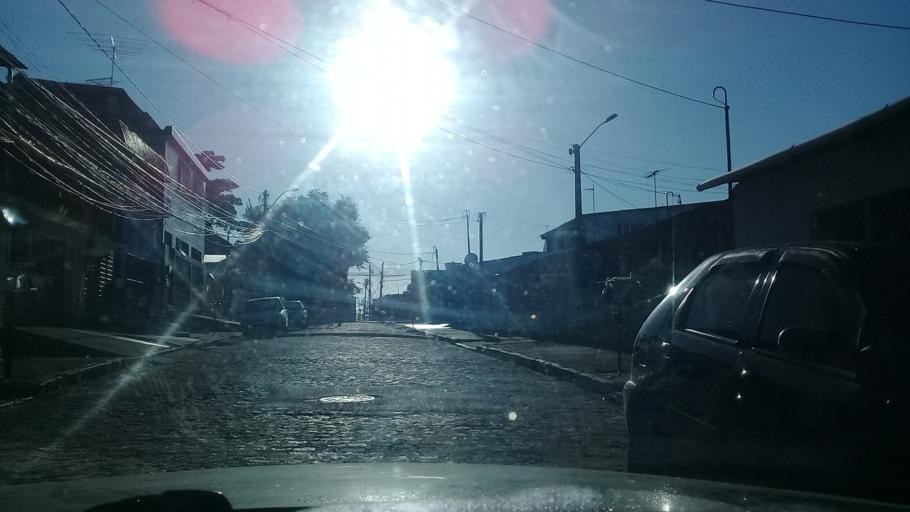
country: BR
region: Pernambuco
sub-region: Jaboatao Dos Guararapes
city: Jaboatao dos Guararapes
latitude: -8.1204
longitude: -34.9562
